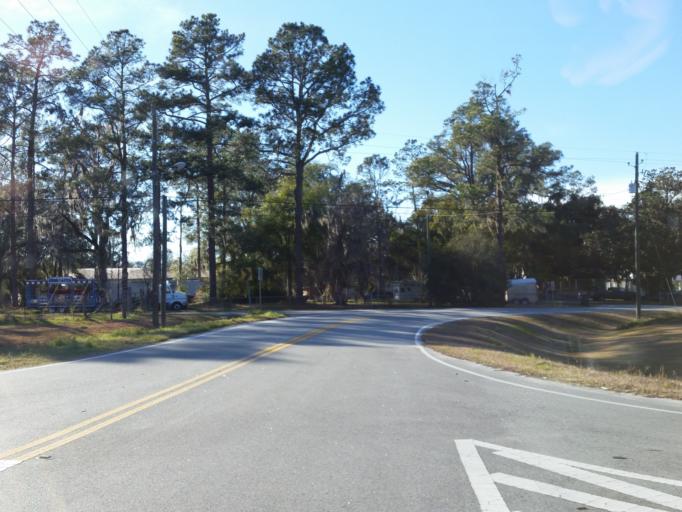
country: US
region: Georgia
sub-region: Lowndes County
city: Valdosta
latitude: 30.7436
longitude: -83.2200
